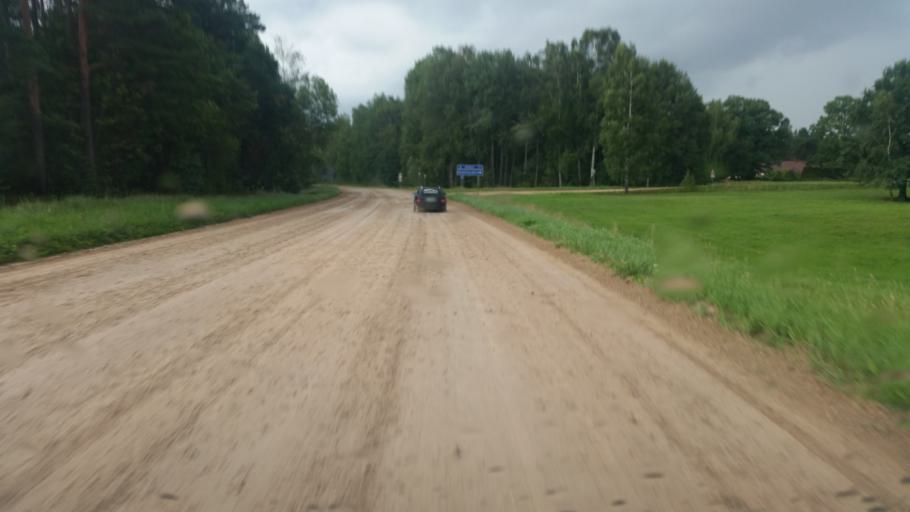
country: LV
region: Vecumnieki
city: Vecumnieki
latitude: 56.4233
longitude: 24.4965
